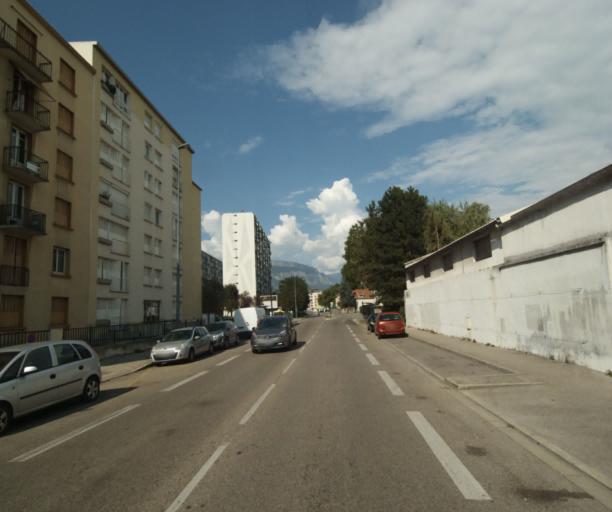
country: FR
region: Rhone-Alpes
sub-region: Departement de l'Isere
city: Grenoble
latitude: 45.1691
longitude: 5.7223
